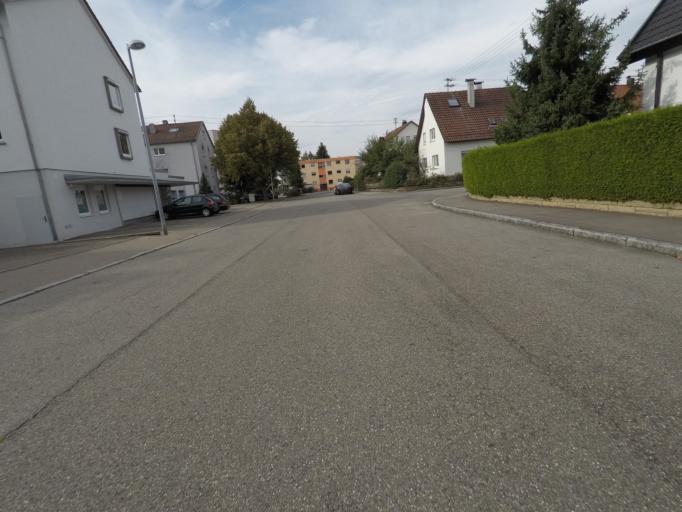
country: DE
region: Baden-Wuerttemberg
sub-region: Regierungsbezirk Stuttgart
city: Ehningen
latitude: 48.6634
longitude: 8.9501
